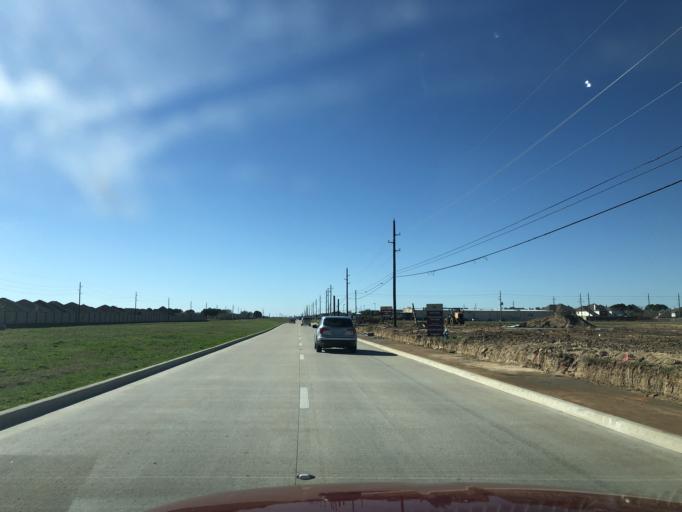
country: US
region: Texas
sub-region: Fort Bend County
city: Fulshear
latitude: 29.6965
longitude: -95.8292
